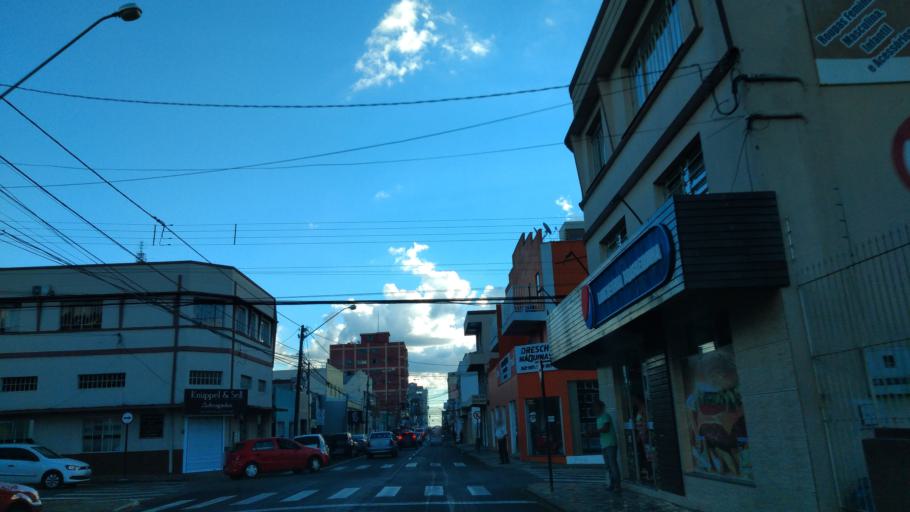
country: BR
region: Parana
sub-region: Guarapuava
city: Guarapuava
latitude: -25.3906
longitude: -51.4664
